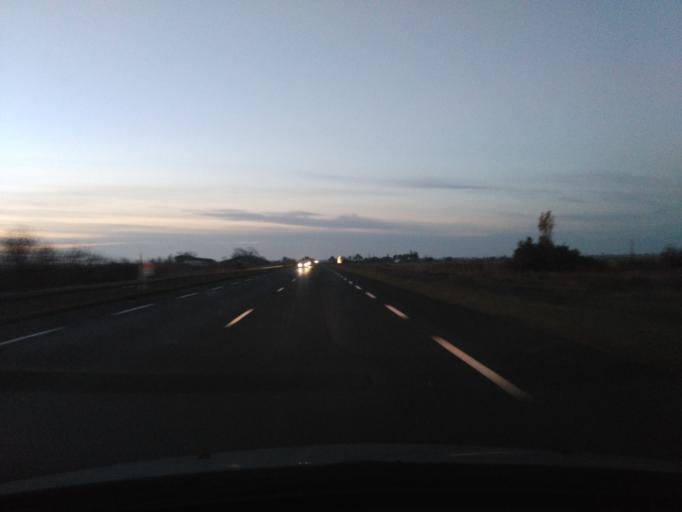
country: FR
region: Pays de la Loire
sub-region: Departement de la Vendee
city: Champagne-les-Marais
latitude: 46.4041
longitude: -1.0972
